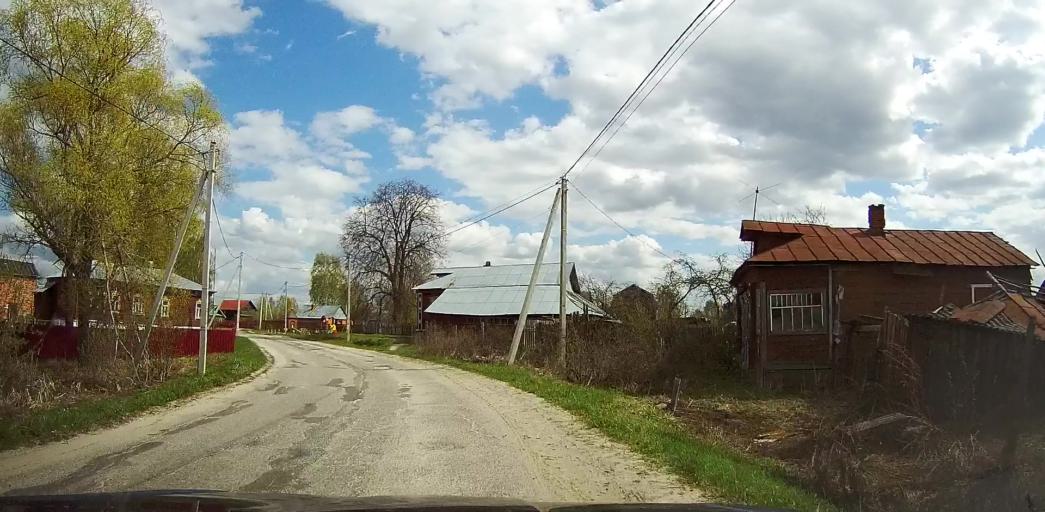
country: RU
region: Moskovskaya
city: Davydovo
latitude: 55.6388
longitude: 38.7782
